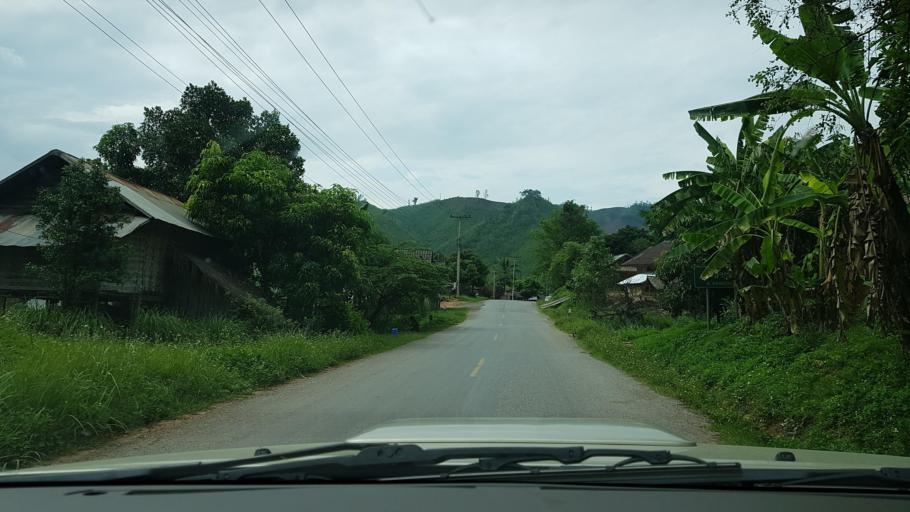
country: LA
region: Loungnamtha
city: Muang Nale
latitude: 20.3645
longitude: 101.7123
